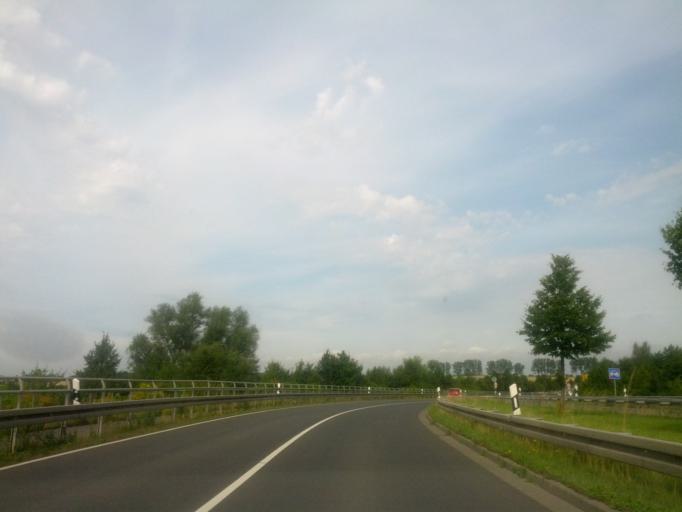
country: DE
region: Mecklenburg-Vorpommern
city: Hornstorf
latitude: 53.8918
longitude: 11.5272
